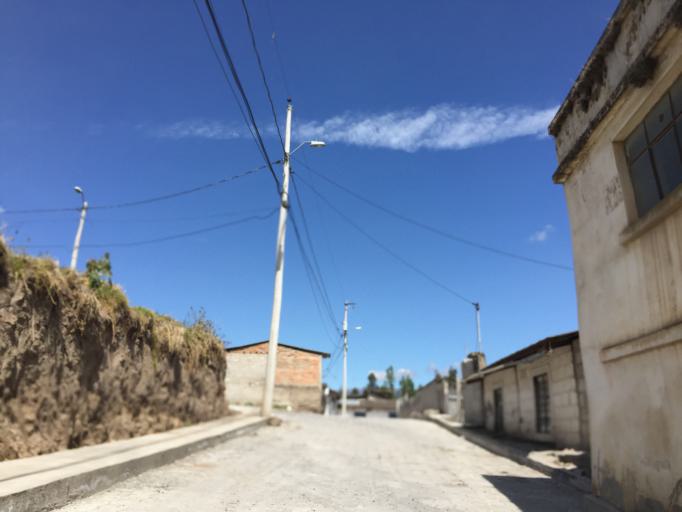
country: EC
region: Imbabura
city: Ibarra
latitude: 0.3155
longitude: -78.1587
